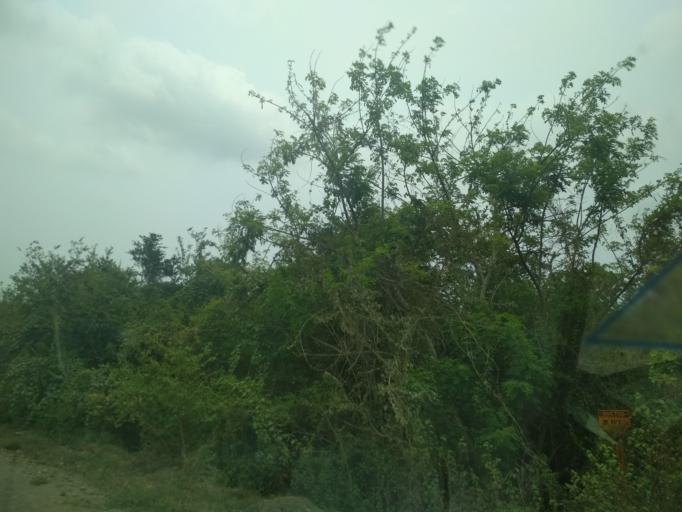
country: MX
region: Veracruz
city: Paso del Toro
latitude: 19.0414
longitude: -96.1490
